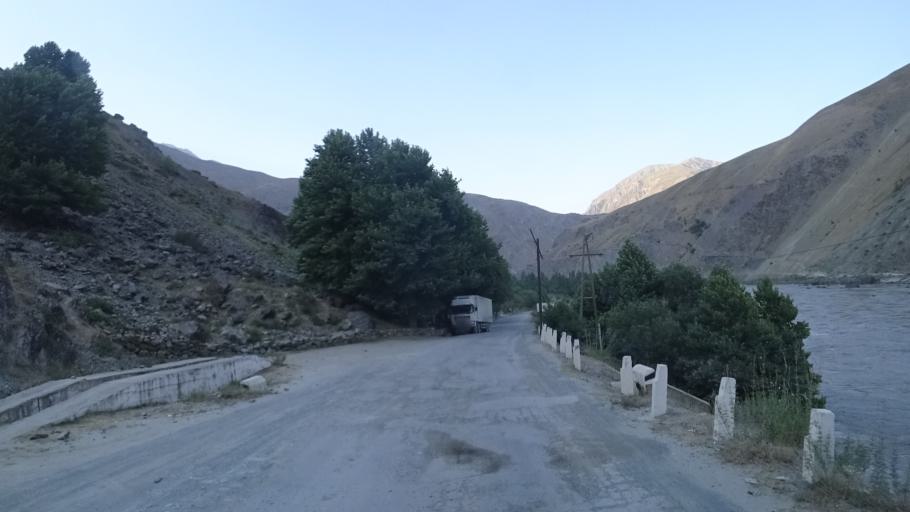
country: TJ
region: Gorno-Badakhshan
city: Qalaikhumb
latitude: 38.4404
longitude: 70.7606
